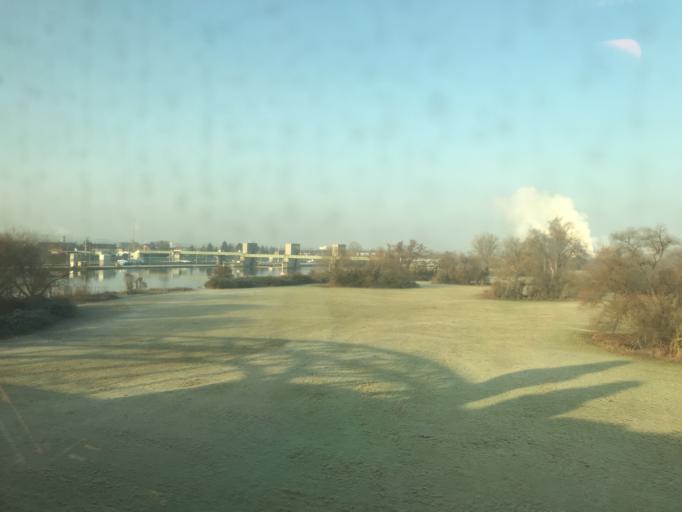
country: DE
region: Hesse
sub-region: Regierungsbezirk Darmstadt
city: Hochheim am Main
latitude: 50.0017
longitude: 8.3397
